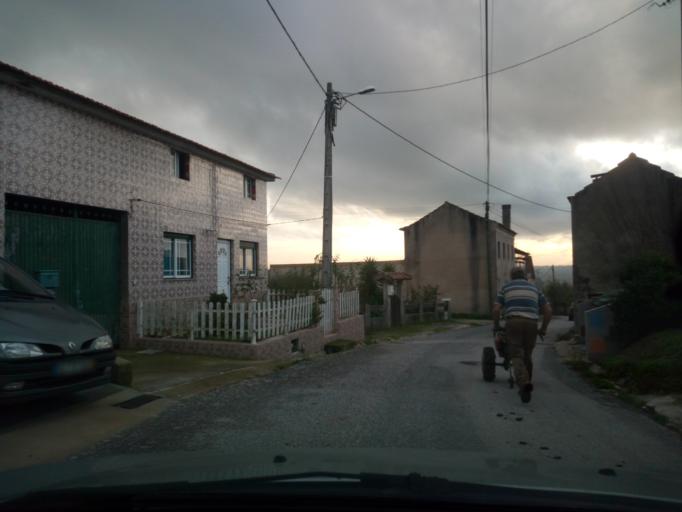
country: PT
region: Aveiro
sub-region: Oliveira do Bairro
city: Oliveira do Bairro
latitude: 40.5429
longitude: -8.4883
